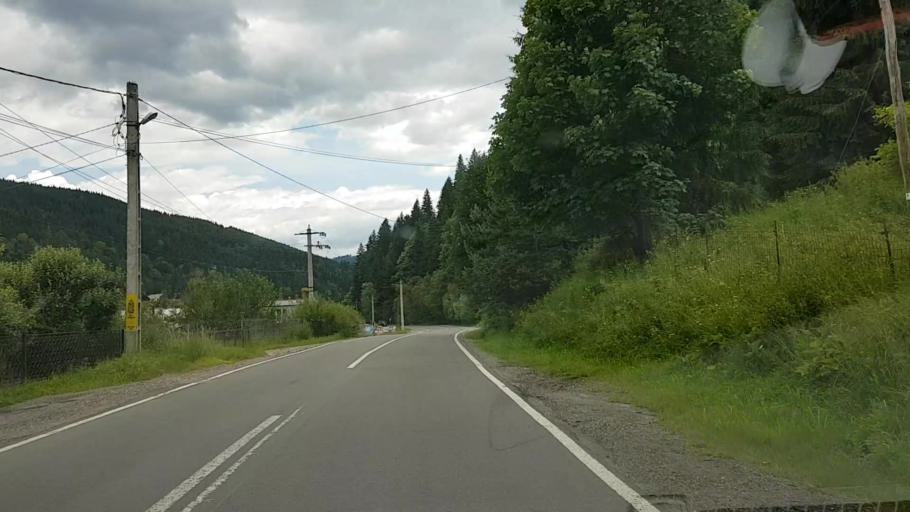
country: RO
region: Neamt
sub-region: Comuna Poiana Teiului
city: Poiana Teiului
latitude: 47.1059
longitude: 25.9345
